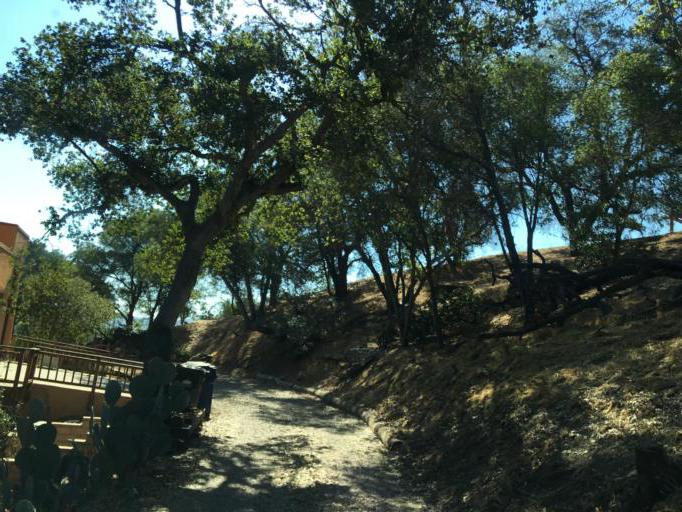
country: US
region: California
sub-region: Los Angeles County
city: Topanga
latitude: 34.1241
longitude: -118.6038
